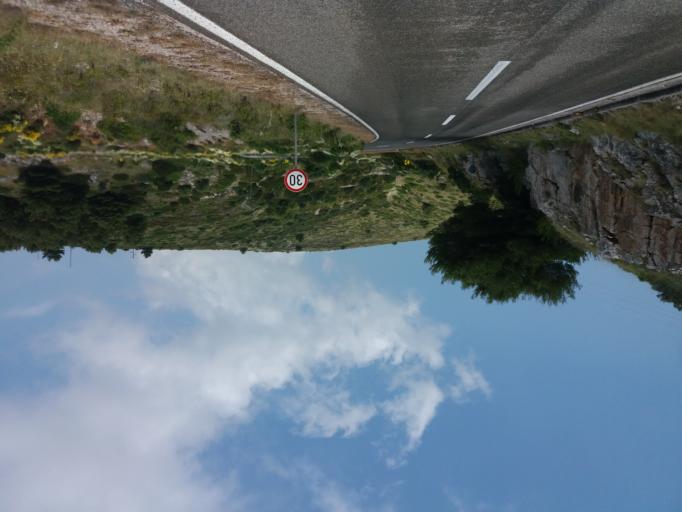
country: HR
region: Zadarska
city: Ugljan
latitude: 44.0483
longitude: 15.0155
